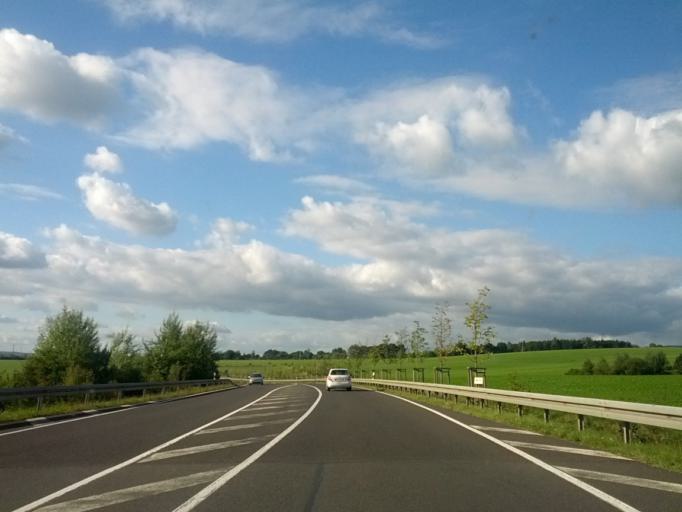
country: DE
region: Thuringia
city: Barchfeld
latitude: 50.8025
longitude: 10.3217
